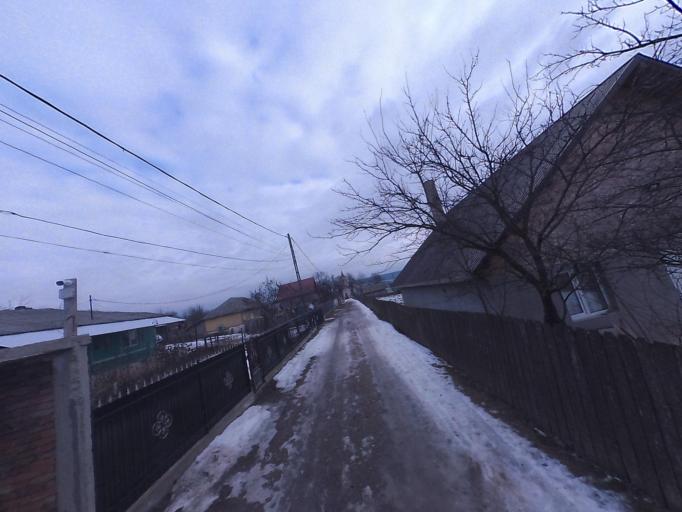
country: RO
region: Iasi
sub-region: Comuna Tibanesti
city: Glodenii Gandului
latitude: 46.9762
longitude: 27.3041
